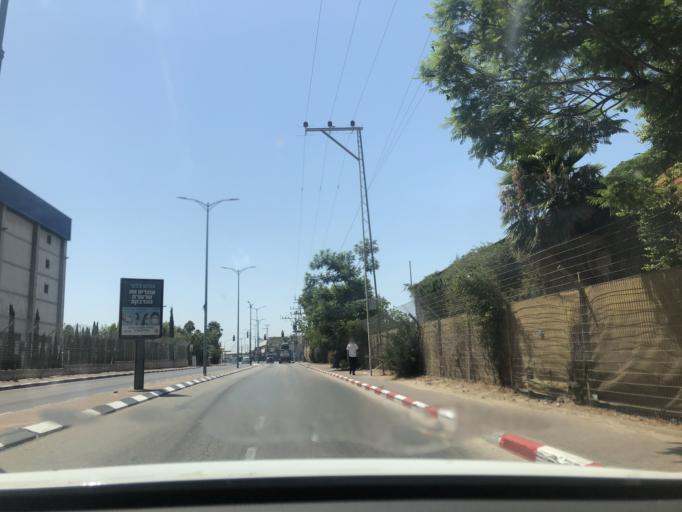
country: IL
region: Central District
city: Lod
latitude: 31.9684
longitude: 34.8976
